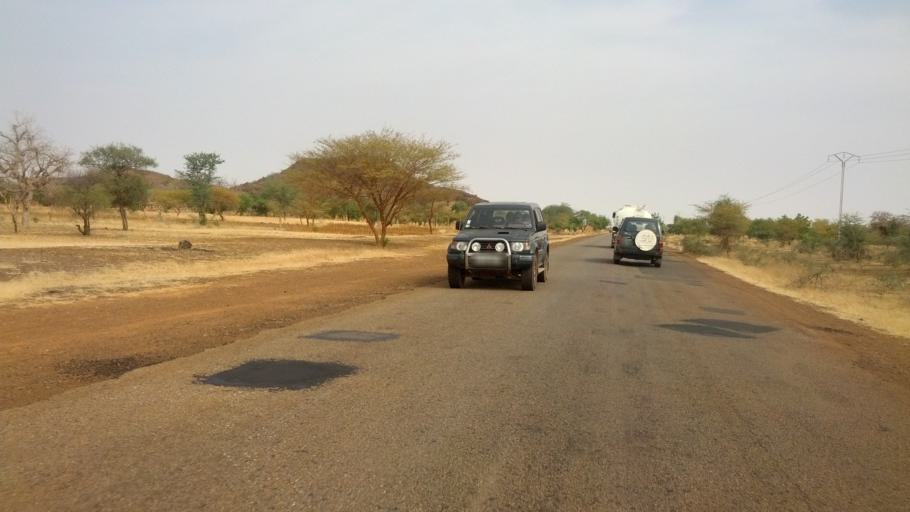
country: BF
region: Centre-Nord
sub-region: Province du Sanmatenga
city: Kaya
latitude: 12.9240
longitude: -1.0776
